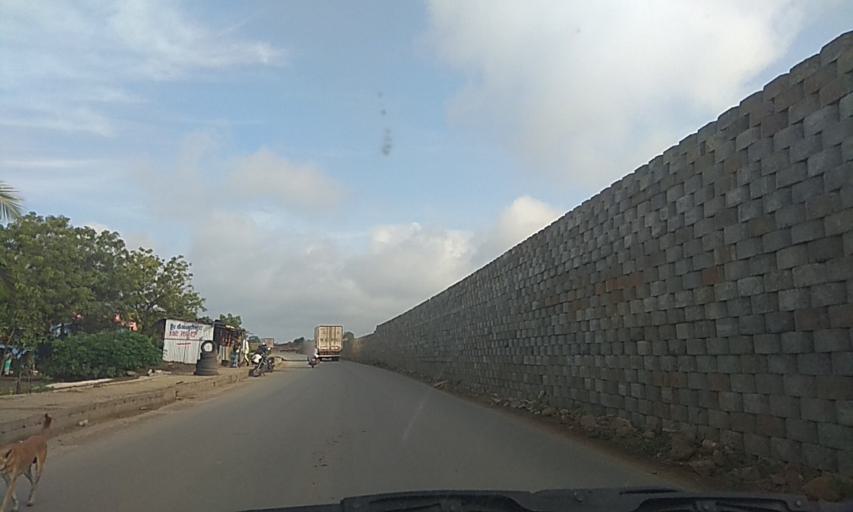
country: IN
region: Karnataka
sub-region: Haveri
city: Savanur
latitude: 14.8714
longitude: 75.3184
